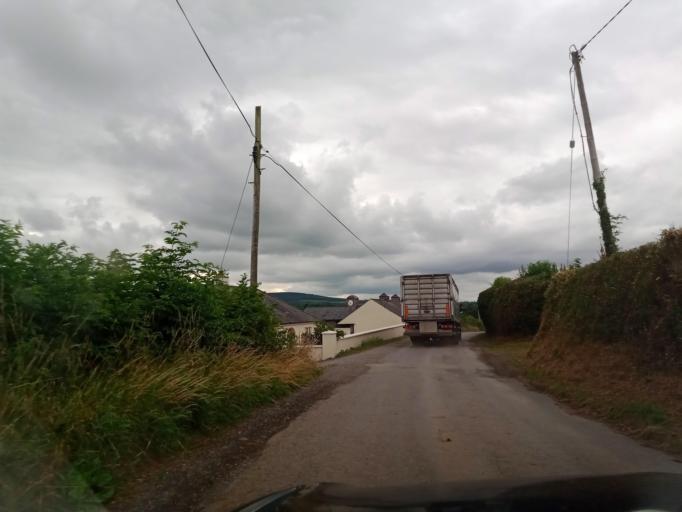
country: IE
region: Leinster
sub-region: Laois
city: Stradbally
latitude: 52.9586
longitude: -7.1928
